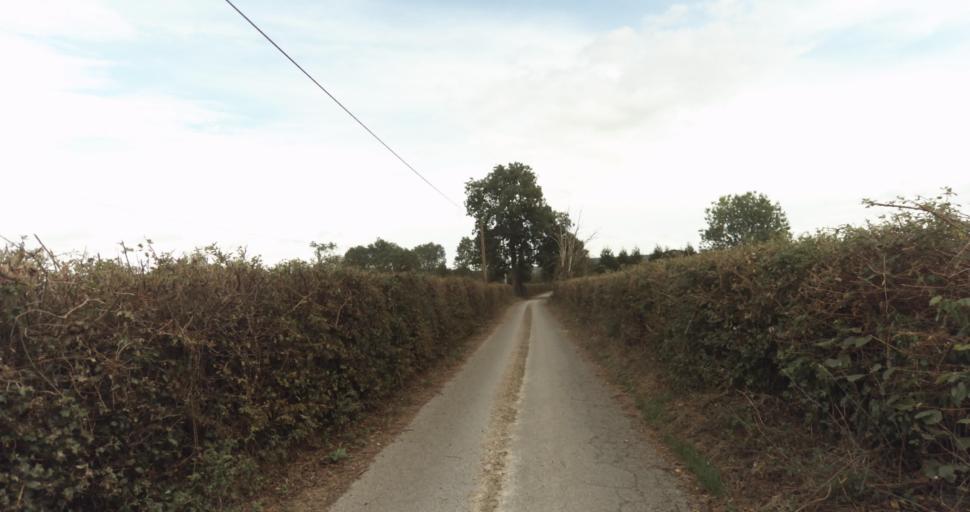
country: FR
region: Lower Normandy
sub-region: Departement de l'Orne
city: Gace
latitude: 48.8652
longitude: 0.2627
